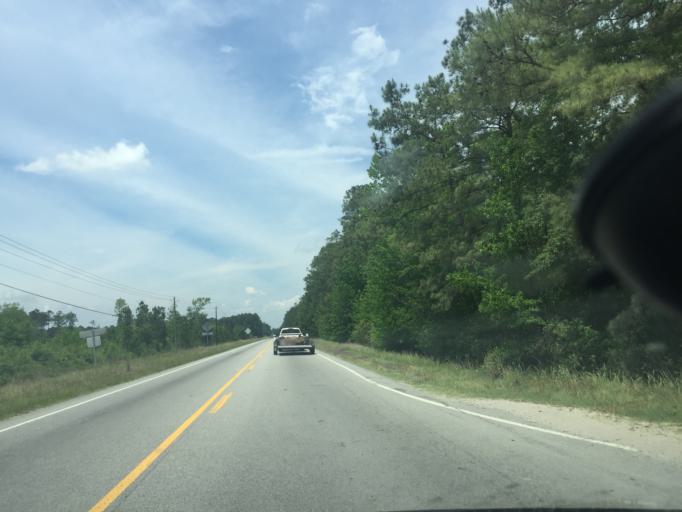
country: US
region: Georgia
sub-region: Chatham County
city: Bloomingdale
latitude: 32.1605
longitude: -81.3693
